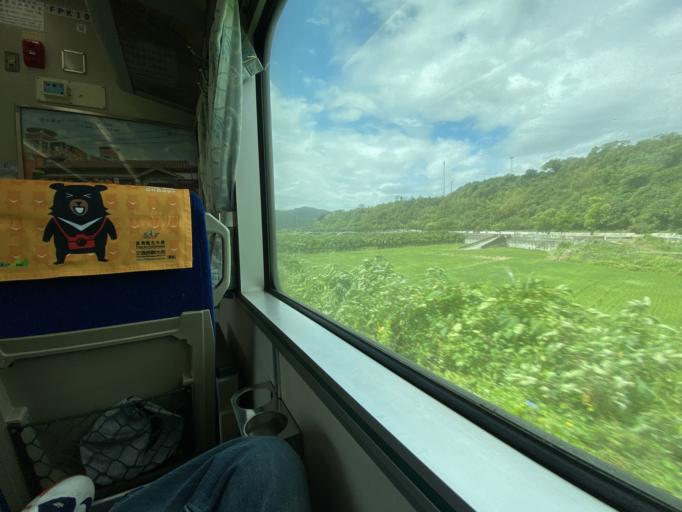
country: TW
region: Taiwan
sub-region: Taitung
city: Taitung
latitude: 22.9012
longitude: 121.1380
